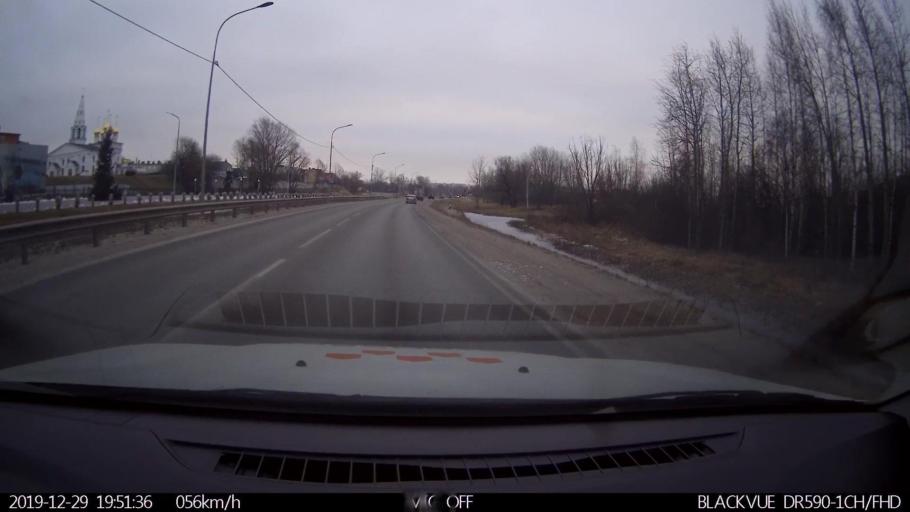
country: RU
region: Nizjnij Novgorod
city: Bor
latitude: 56.3593
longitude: 44.0440
